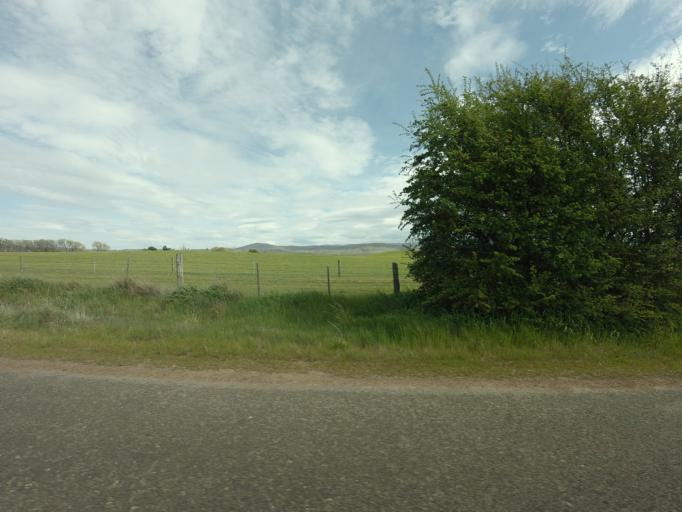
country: AU
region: Tasmania
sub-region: Northern Midlands
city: Evandale
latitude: -41.8764
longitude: 147.3570
